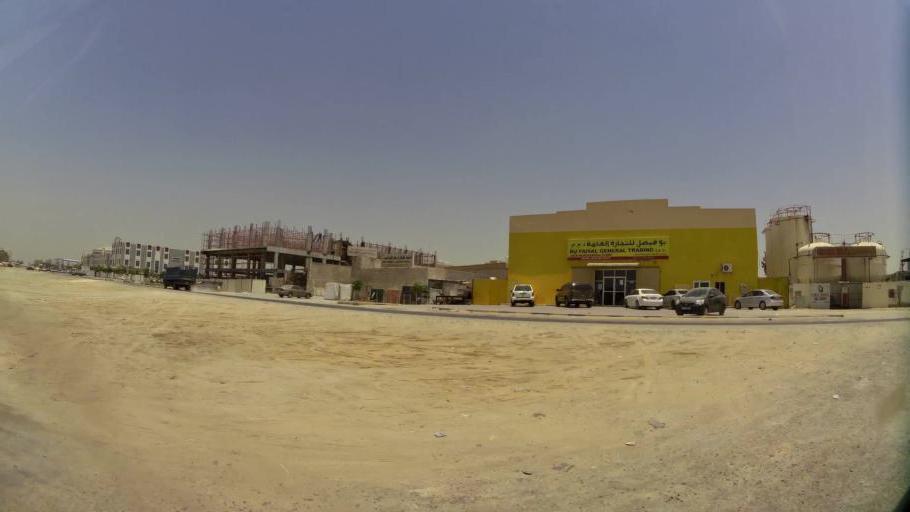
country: AE
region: Ajman
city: Ajman
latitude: 25.3984
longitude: 55.4988
